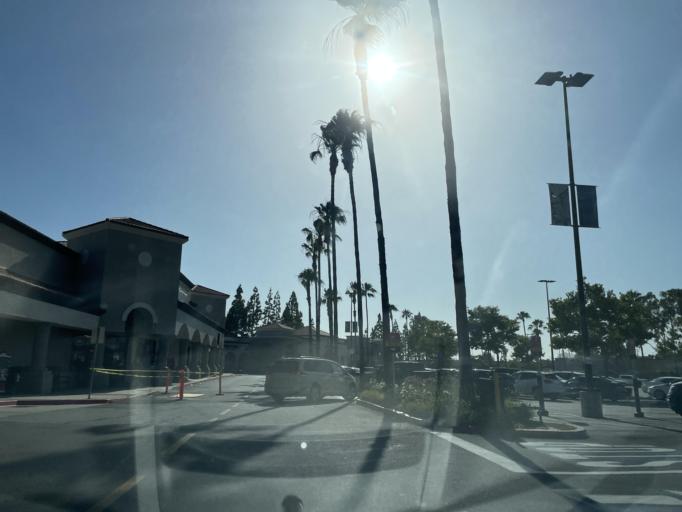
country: US
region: California
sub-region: Los Angeles County
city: La Mirada
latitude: 33.8974
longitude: -118.0072
